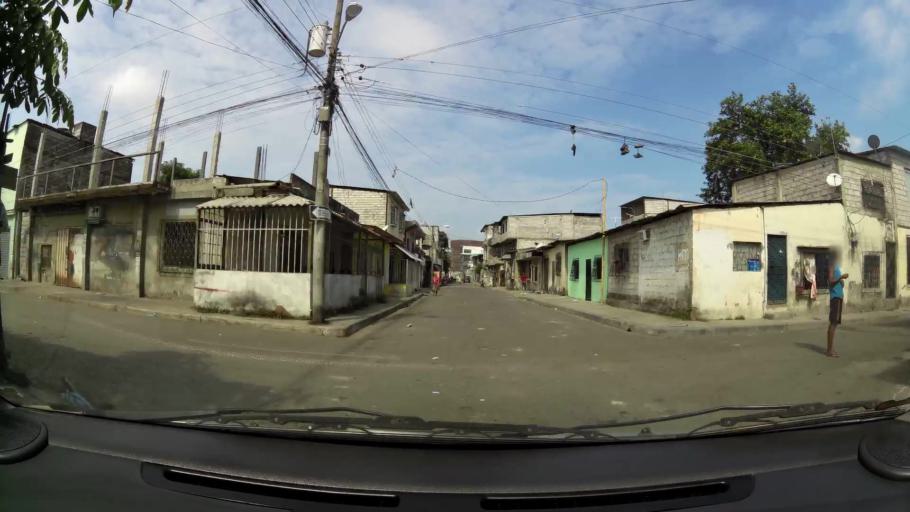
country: EC
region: Guayas
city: Guayaquil
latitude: -2.2745
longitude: -79.8934
